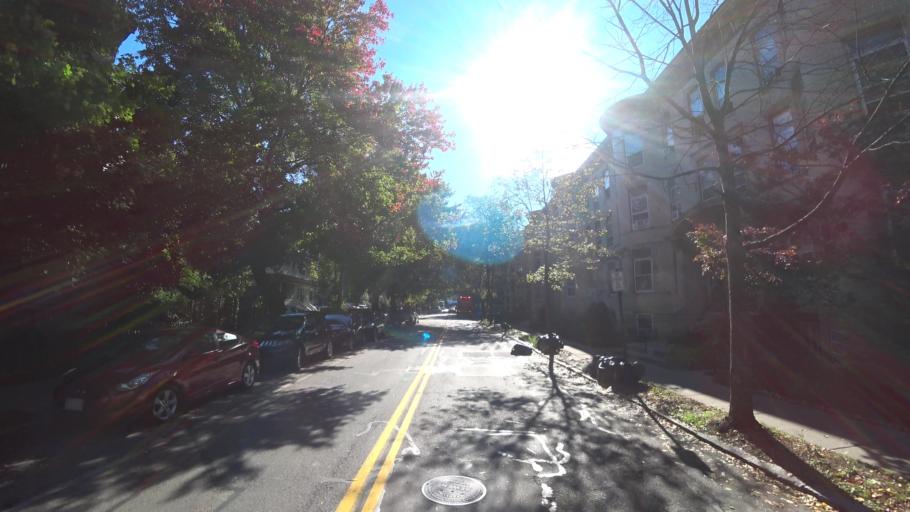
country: US
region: Massachusetts
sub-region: Norfolk County
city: Brookline
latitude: 42.3424
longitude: -71.1263
